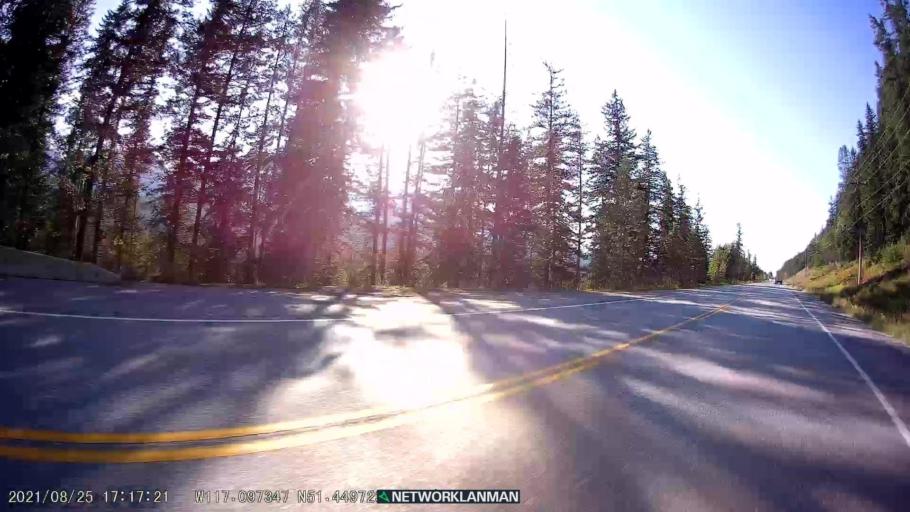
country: CA
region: British Columbia
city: Golden
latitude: 51.4501
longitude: -117.0979
